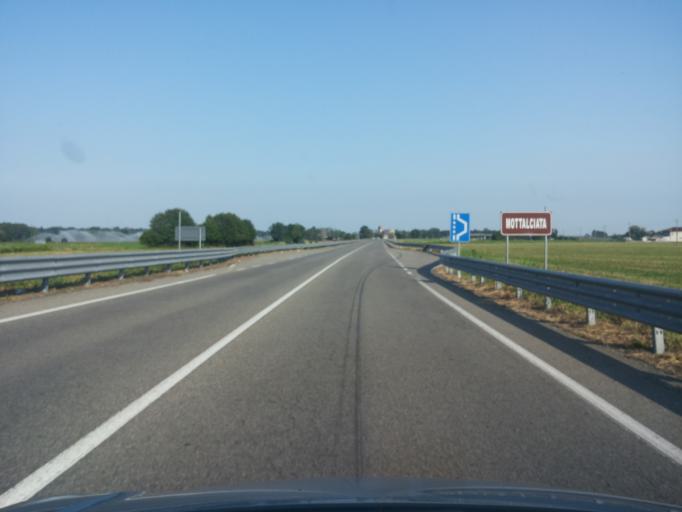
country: IT
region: Piedmont
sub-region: Provincia di Biella
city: Castelletto Cervo
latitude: 45.5254
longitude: 8.1982
